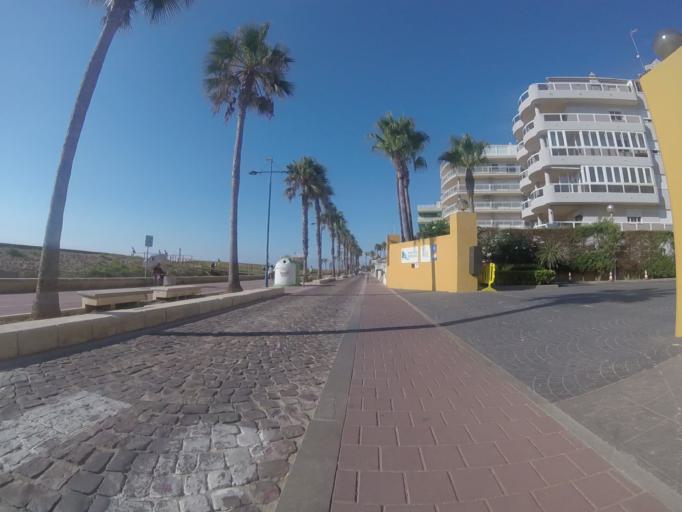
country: ES
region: Valencia
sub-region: Provincia de Castello
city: Benicarlo
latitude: 40.3920
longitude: 0.4130
